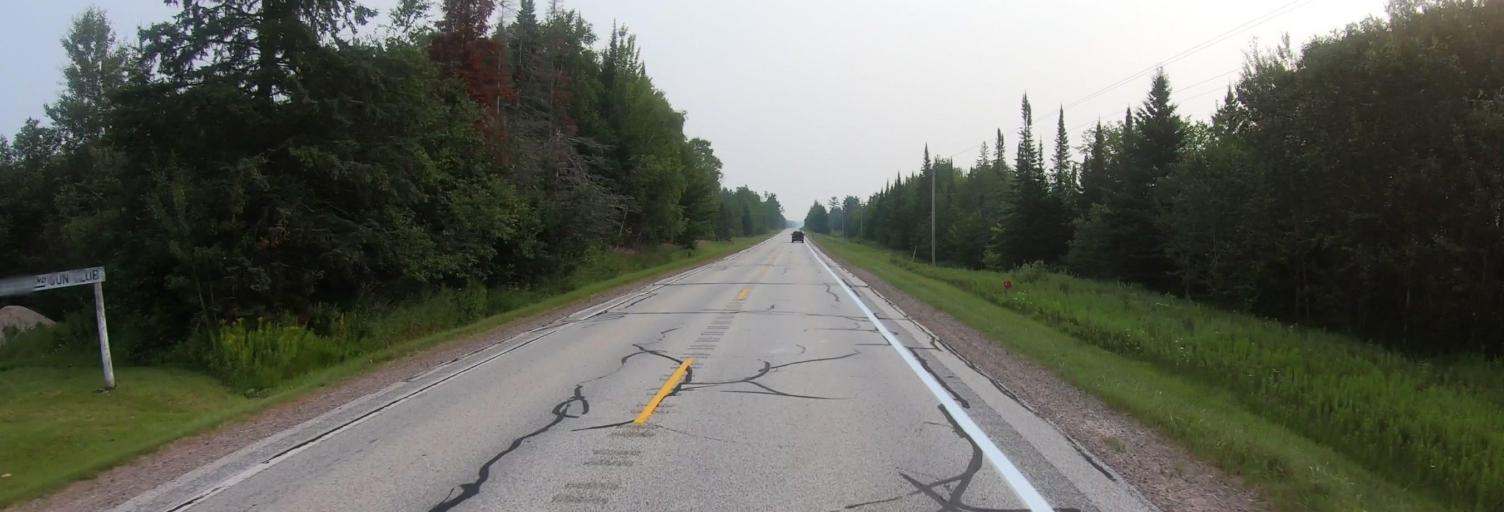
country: US
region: Michigan
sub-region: Luce County
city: Newberry
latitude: 46.5125
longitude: -85.0880
